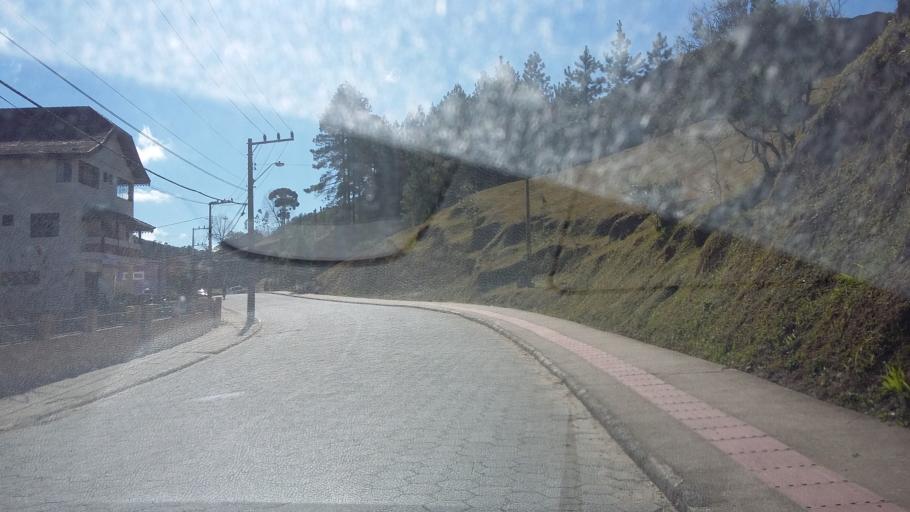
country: BR
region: Santa Catarina
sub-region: Santo Amaro Da Imperatriz
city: Santo Amaro da Imperatriz
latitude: -27.6760
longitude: -49.0108
